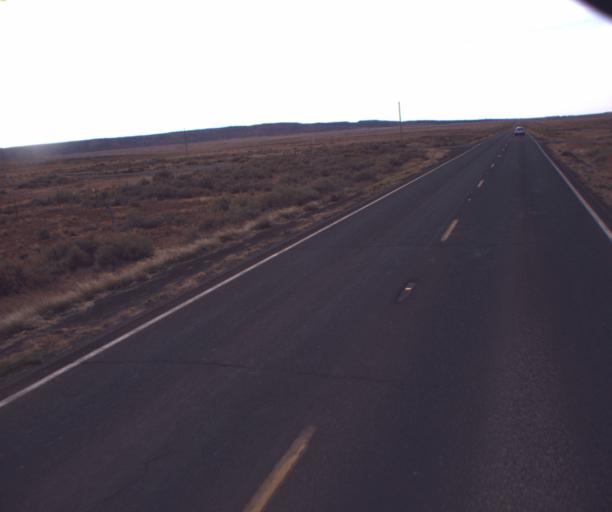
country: US
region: Arizona
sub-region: Apache County
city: Ganado
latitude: 35.8073
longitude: -109.6116
